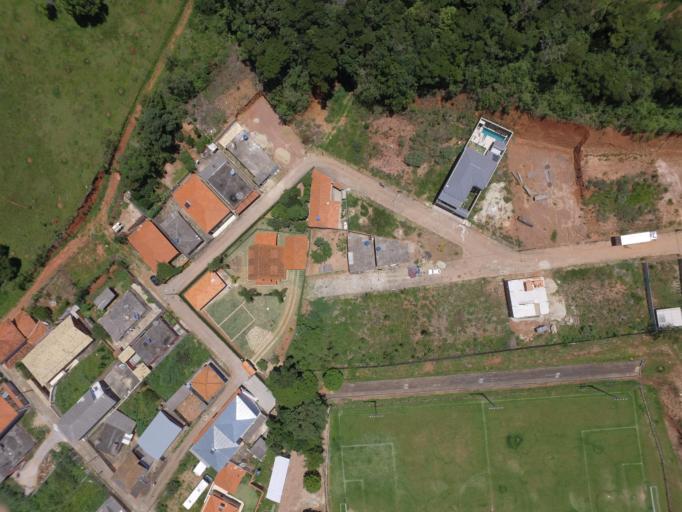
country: BR
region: Minas Gerais
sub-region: Tiradentes
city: Tiradentes
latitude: -21.0643
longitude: -44.0783
